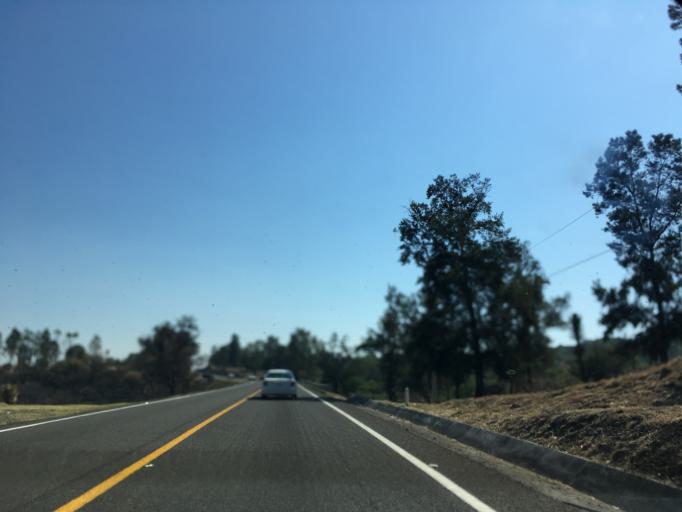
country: MX
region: Michoacan
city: Charo
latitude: 19.7720
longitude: -101.0173
